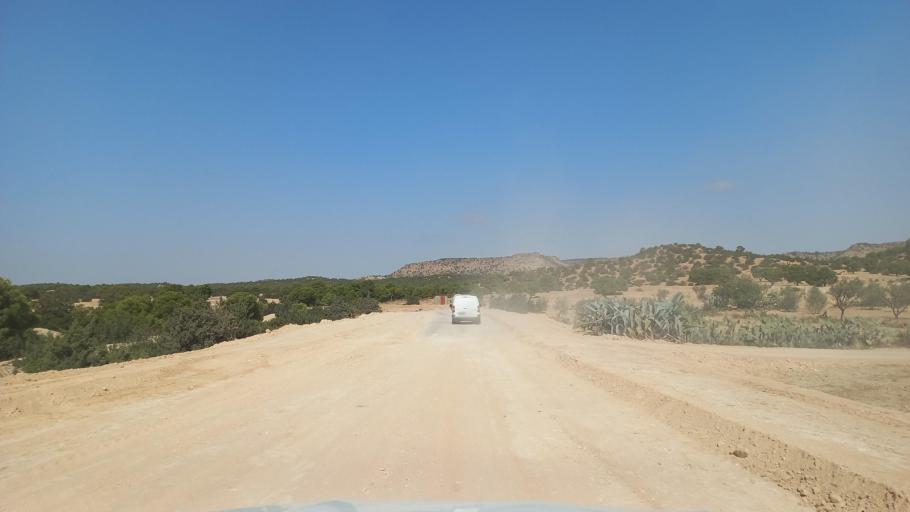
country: TN
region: Al Qasrayn
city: Sbiba
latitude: 35.4062
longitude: 8.9876
